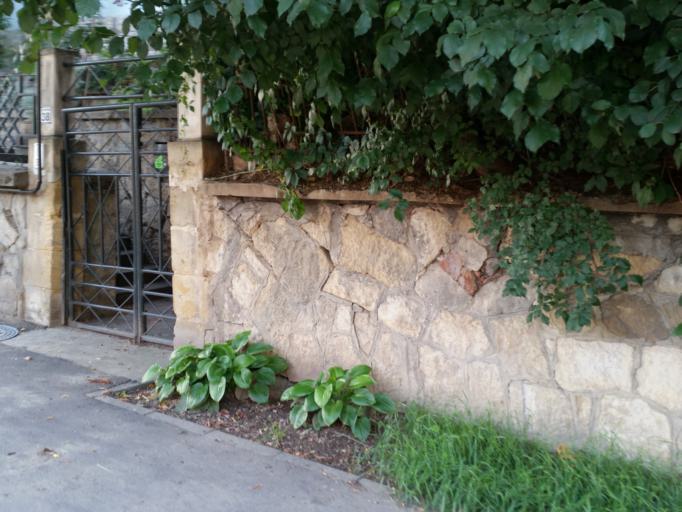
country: RO
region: Cluj
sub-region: Municipiul Cluj-Napoca
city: Cluj-Napoca
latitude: 46.7727
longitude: 23.5747
